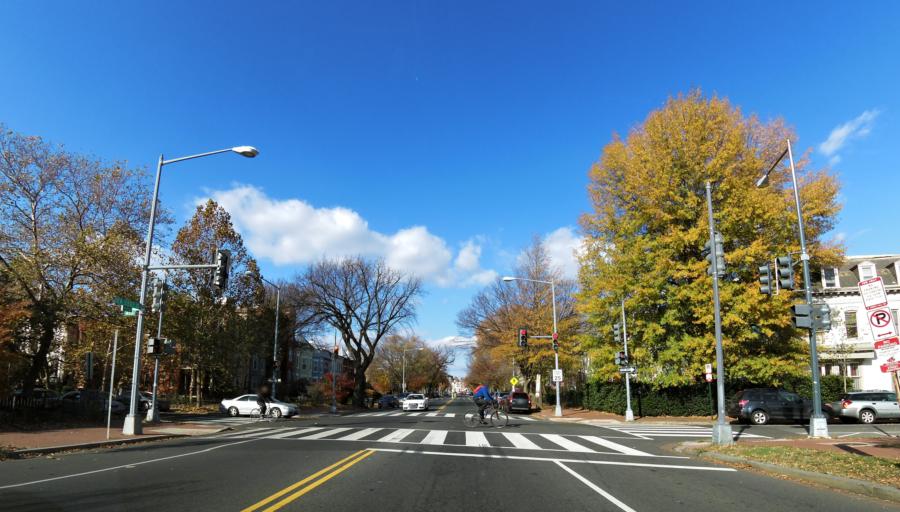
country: US
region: Washington, D.C.
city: Washington, D.C.
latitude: 38.9109
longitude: -77.0168
